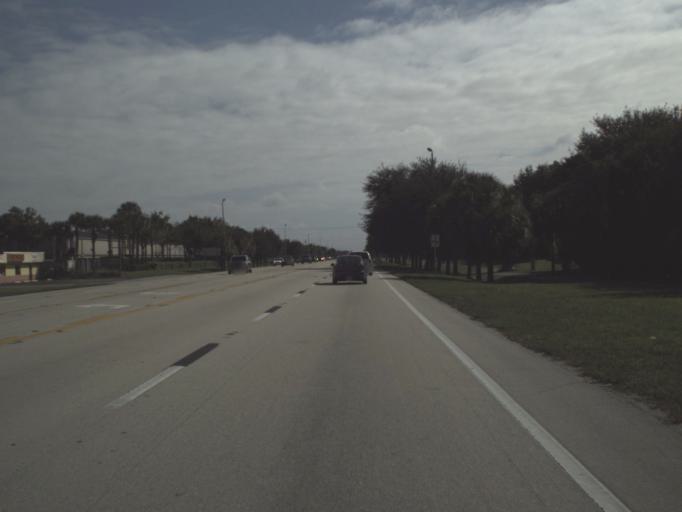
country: US
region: Florida
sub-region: Lee County
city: Fort Myers Shores
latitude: 26.7039
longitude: -81.7500
